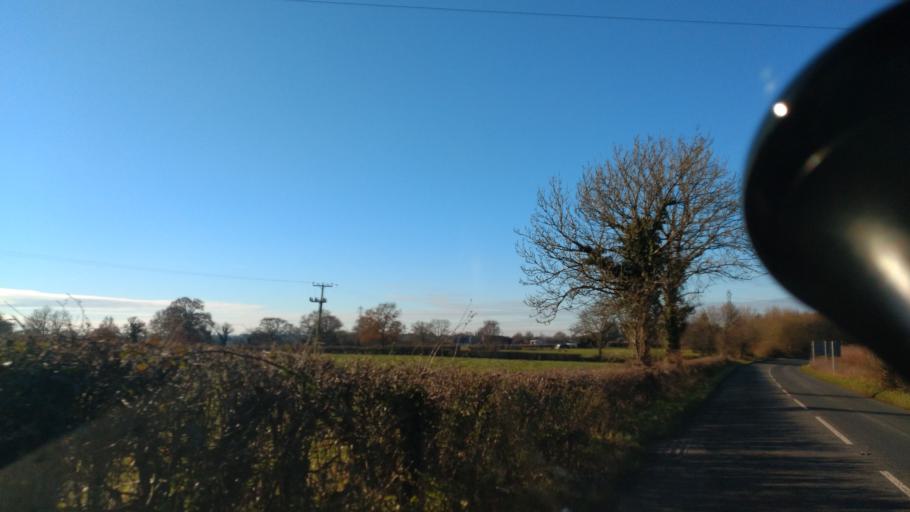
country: GB
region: England
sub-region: Wiltshire
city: Chapmanslade
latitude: 51.2369
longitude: -2.2817
